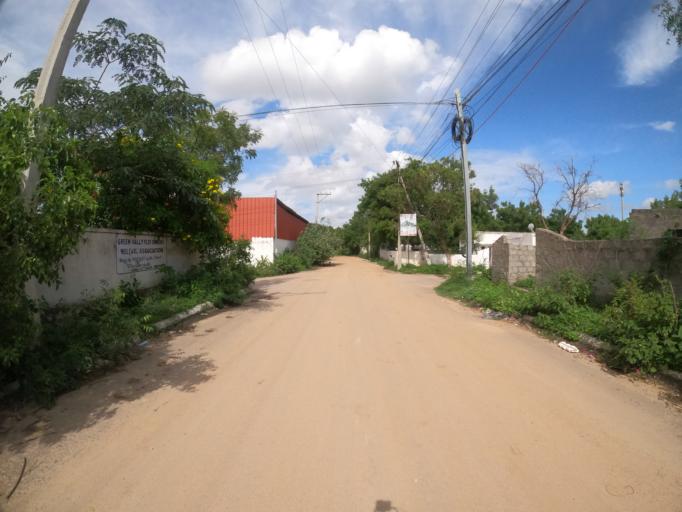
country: IN
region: Telangana
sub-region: Hyderabad
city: Hyderabad
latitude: 17.3515
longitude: 78.3975
